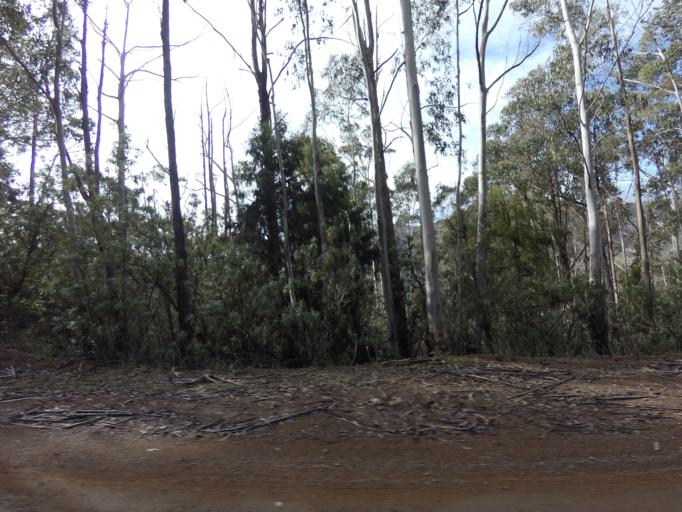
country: AU
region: Tasmania
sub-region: Derwent Valley
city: New Norfolk
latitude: -42.7890
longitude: 146.9373
